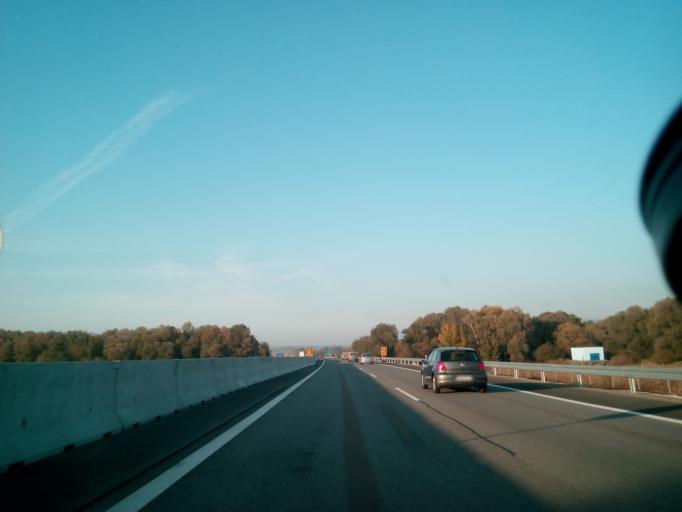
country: SK
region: Kosicky
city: Kosice
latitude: 48.8161
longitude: 21.3103
